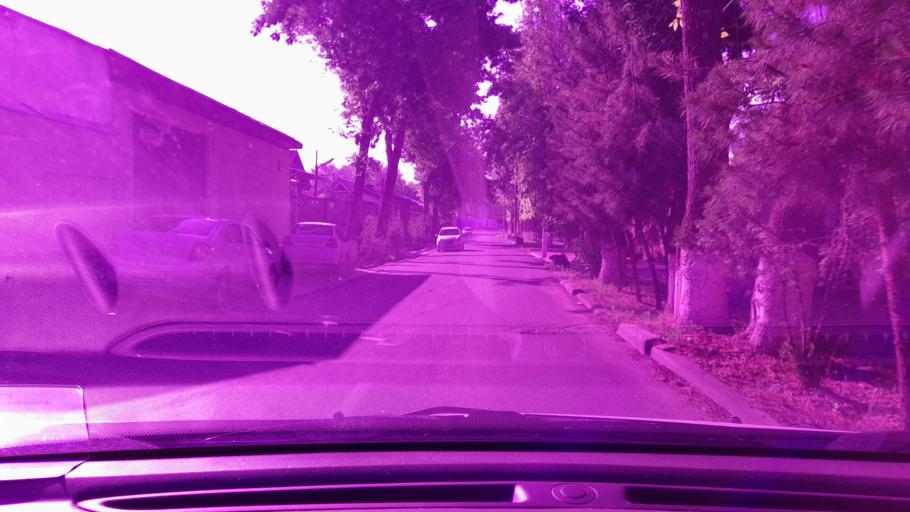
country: UZ
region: Toshkent
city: Salor
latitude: 41.3338
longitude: 69.3614
